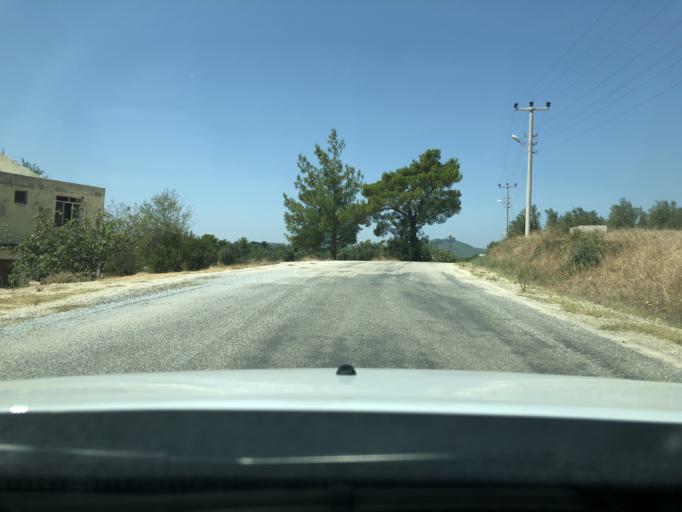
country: TR
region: Antalya
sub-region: Manavgat
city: Kizilagac
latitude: 36.8562
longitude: 31.5645
